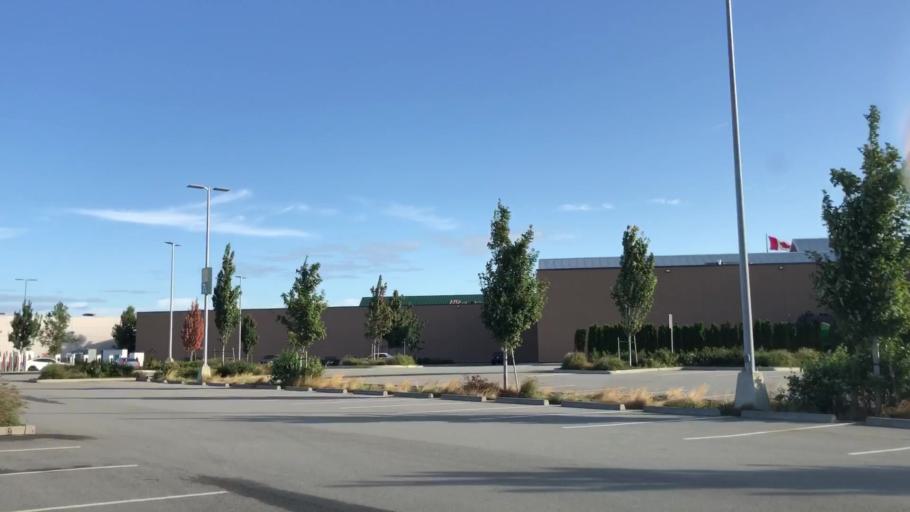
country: US
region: Washington
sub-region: Whatcom County
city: Point Roberts
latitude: 49.0372
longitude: -123.0826
